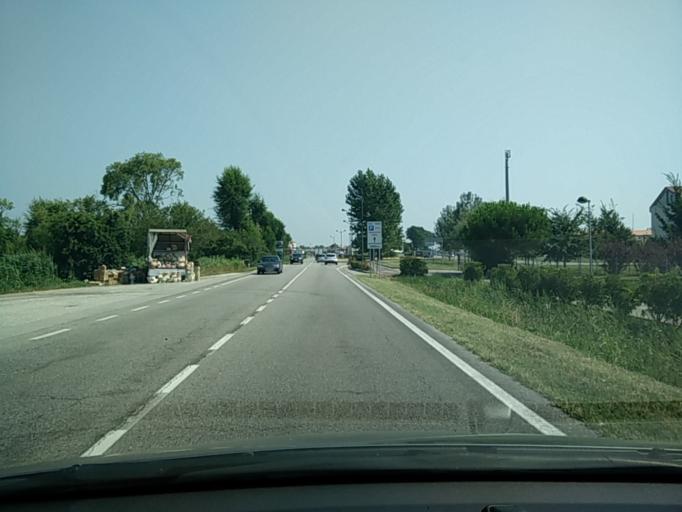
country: IT
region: Veneto
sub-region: Provincia di Venezia
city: Caorle
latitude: 45.5990
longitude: 12.8668
